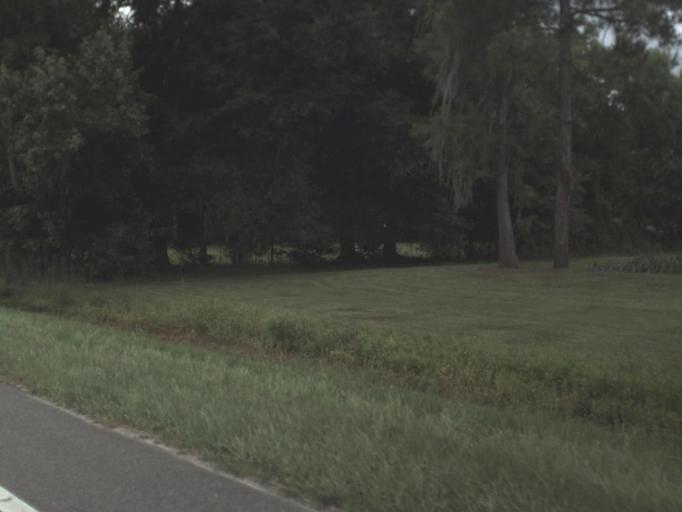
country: US
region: Florida
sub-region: Bradford County
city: Starke
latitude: 29.9245
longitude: -82.0992
